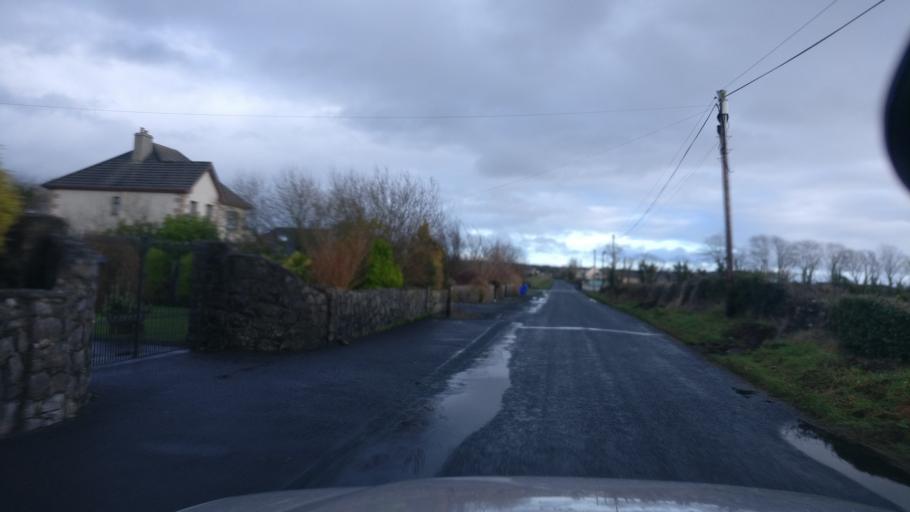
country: IE
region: Connaught
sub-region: County Galway
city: Athenry
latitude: 53.2957
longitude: -8.6845
